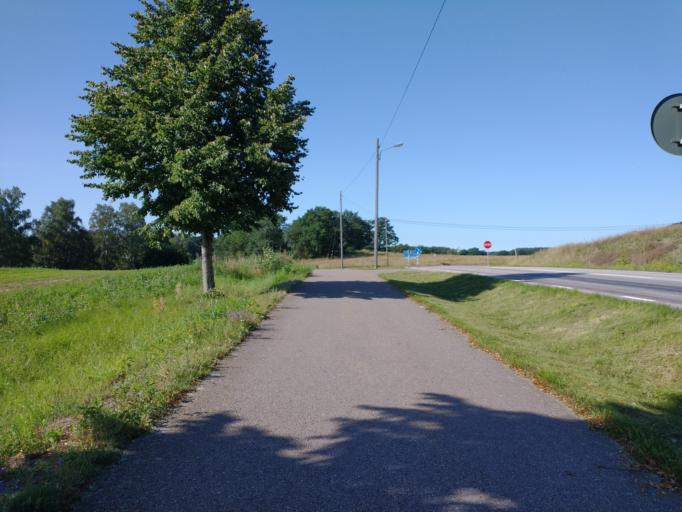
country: SE
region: Kalmar
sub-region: Kalmar Kommun
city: Lindsdal
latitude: 56.7801
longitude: 16.2856
